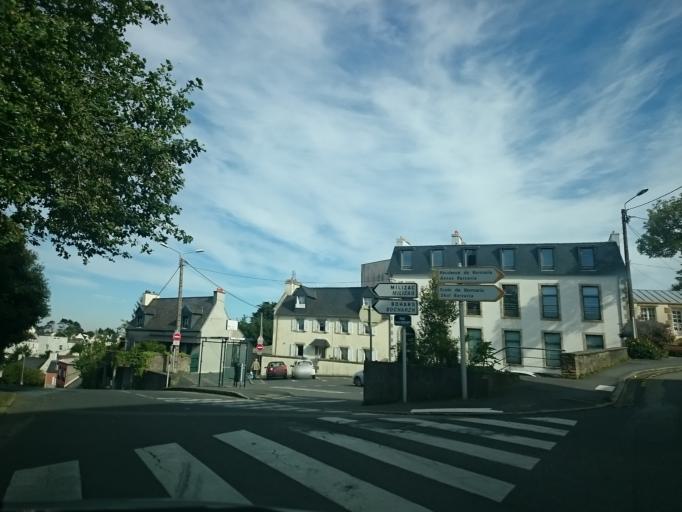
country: FR
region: Brittany
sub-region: Departement du Finistere
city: Brest
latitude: 48.4167
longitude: -4.4925
